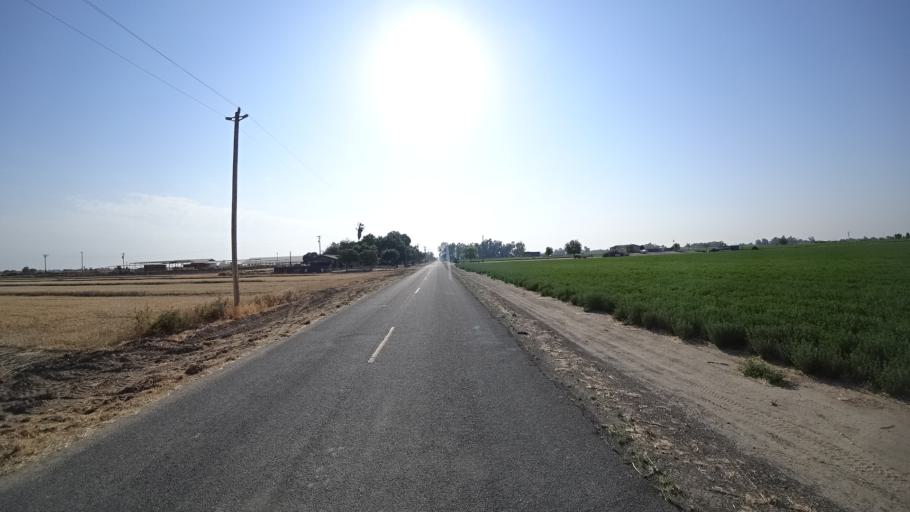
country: US
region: California
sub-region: Fresno County
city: Riverdale
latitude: 36.3584
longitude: -119.8821
